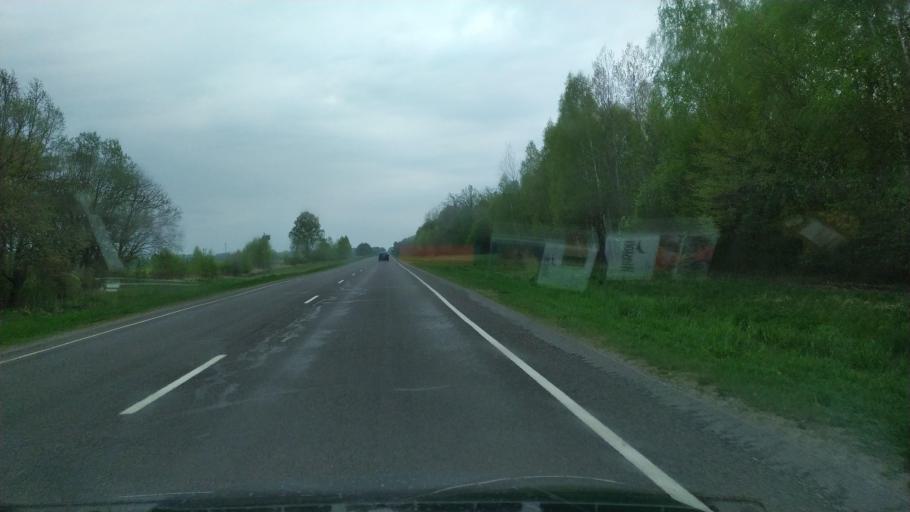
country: BY
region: Brest
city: Horad Kobryn
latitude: 52.3167
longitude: 24.5518
